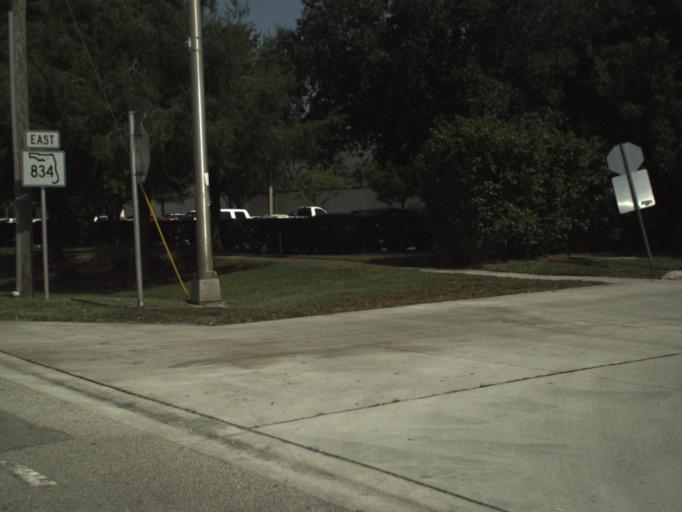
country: US
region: Florida
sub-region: Broward County
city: Tedder
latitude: 26.2744
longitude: -80.1512
